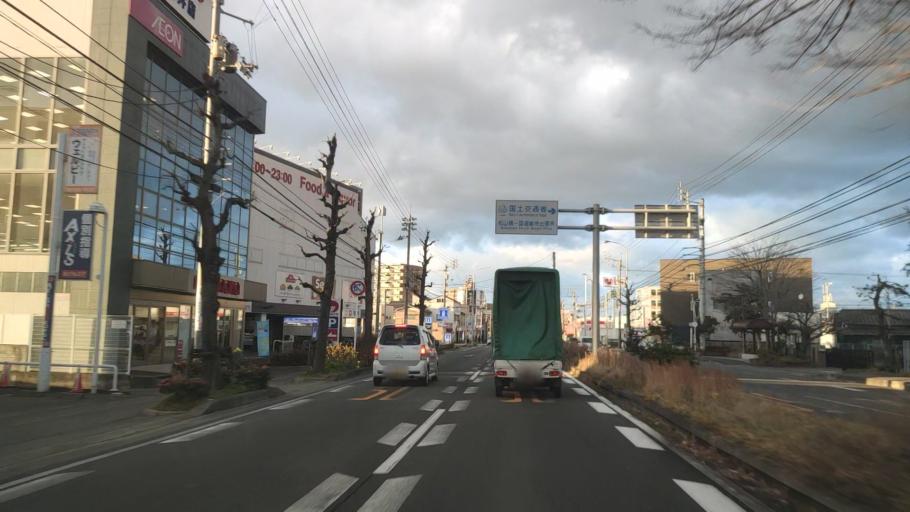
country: JP
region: Ehime
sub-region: Shikoku-chuo Shi
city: Matsuyama
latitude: 33.8127
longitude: 132.7785
